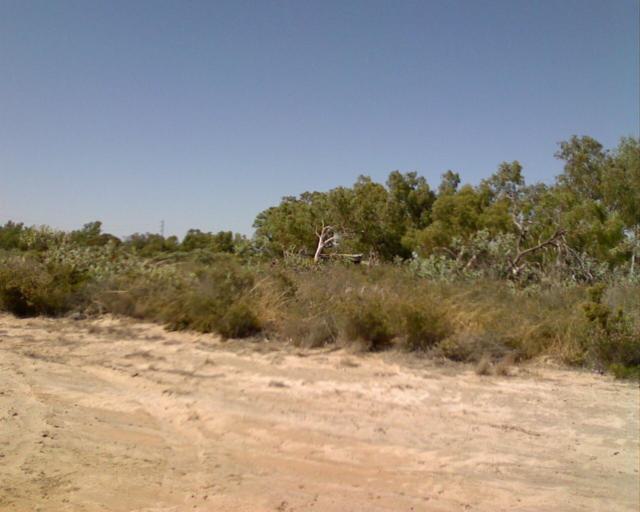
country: AU
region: Western Australia
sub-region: Dandaragan
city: Jurien Bay
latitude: -29.8150
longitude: 115.2677
